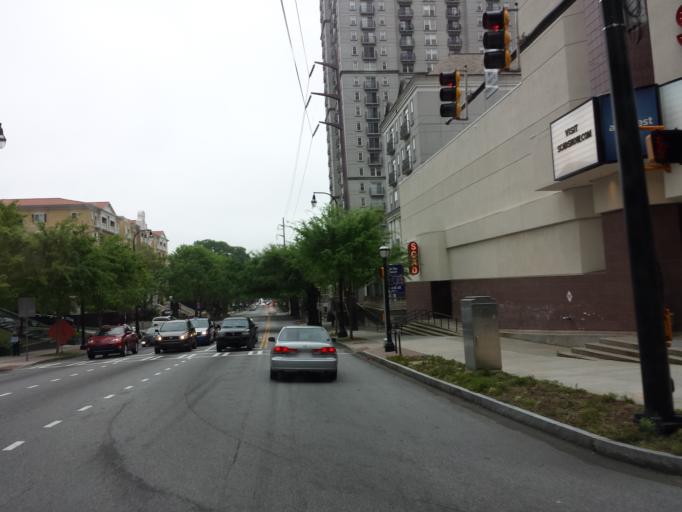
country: US
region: Georgia
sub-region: Fulton County
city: Atlanta
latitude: 33.7864
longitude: -84.3820
